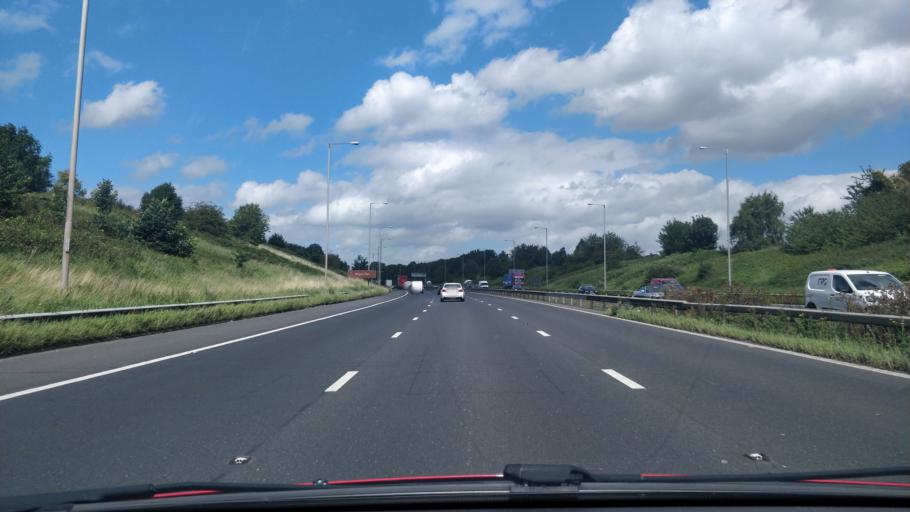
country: GB
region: England
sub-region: Borough of Wigan
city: Ashton in Makerfield
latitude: 53.4959
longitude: -2.6570
